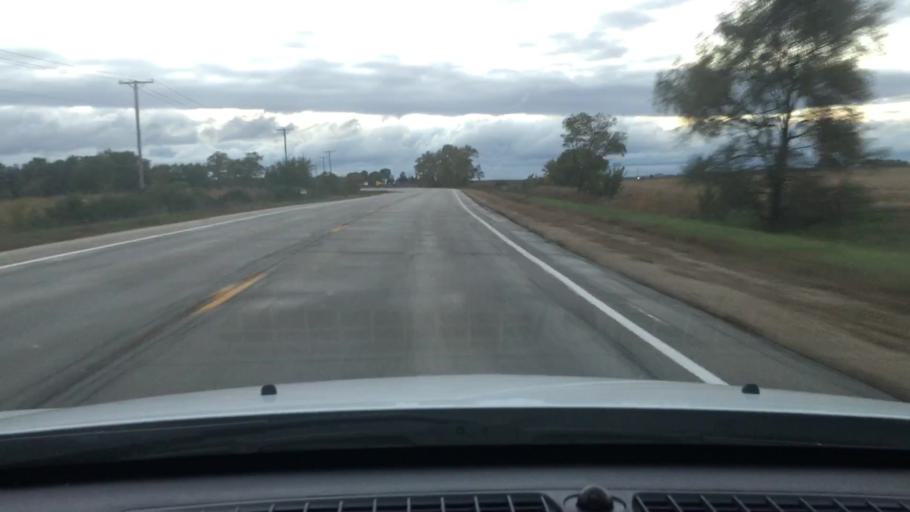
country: US
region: Illinois
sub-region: DeKalb County
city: DeKalb
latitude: 41.9350
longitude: -88.8052
